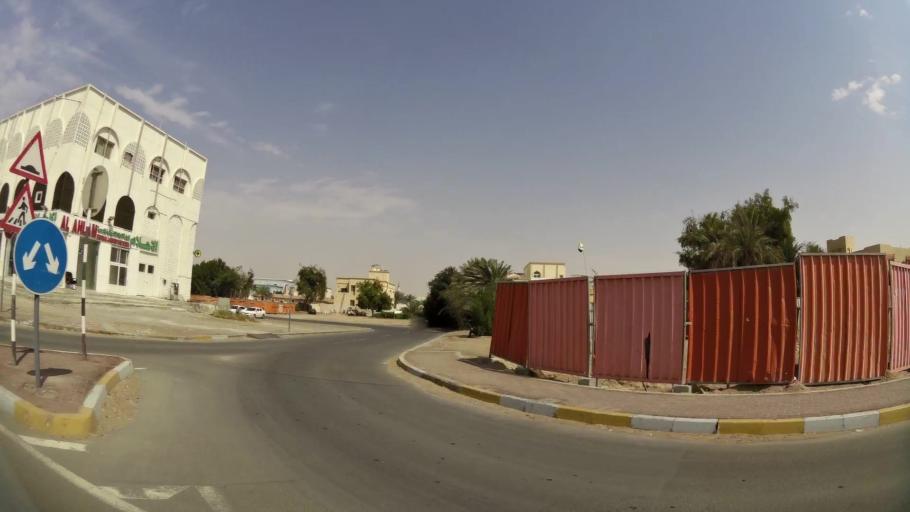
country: AE
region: Abu Dhabi
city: Abu Dhabi
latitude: 24.2915
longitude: 54.6353
